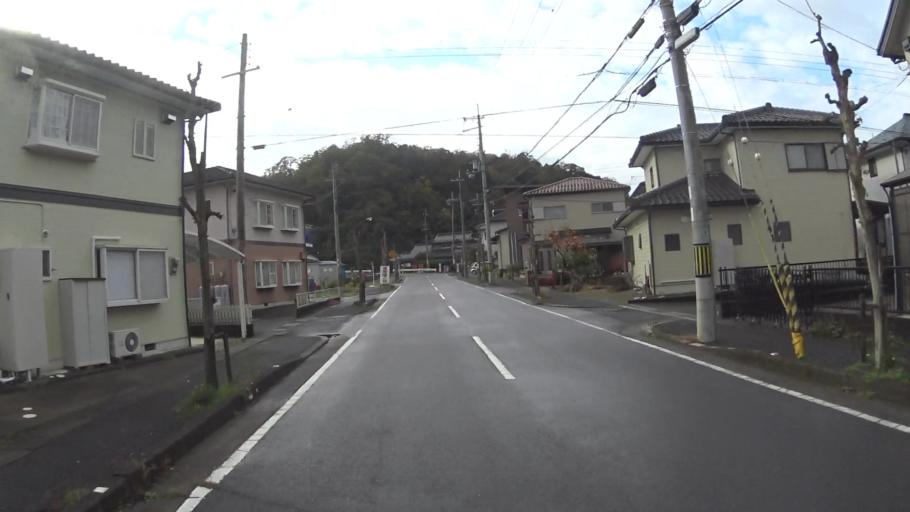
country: JP
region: Kyoto
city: Ayabe
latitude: 35.2964
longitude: 135.2348
